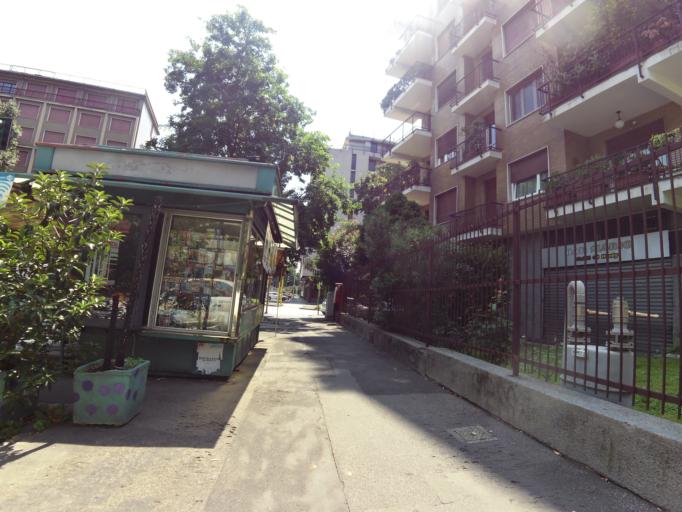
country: IT
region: Lombardy
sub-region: Citta metropolitana di Milano
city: Milano
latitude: 45.4854
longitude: 9.1516
